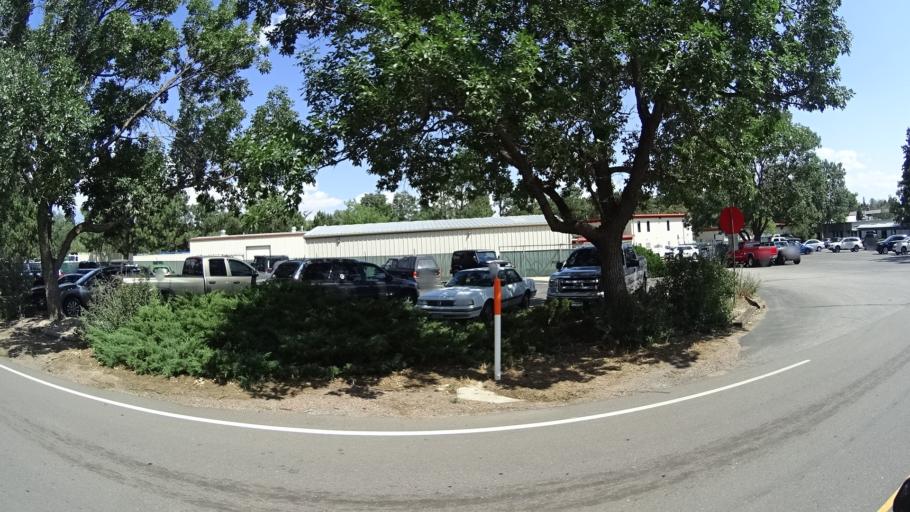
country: US
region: Colorado
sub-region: El Paso County
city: Colorado Springs
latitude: 38.8543
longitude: -104.8316
